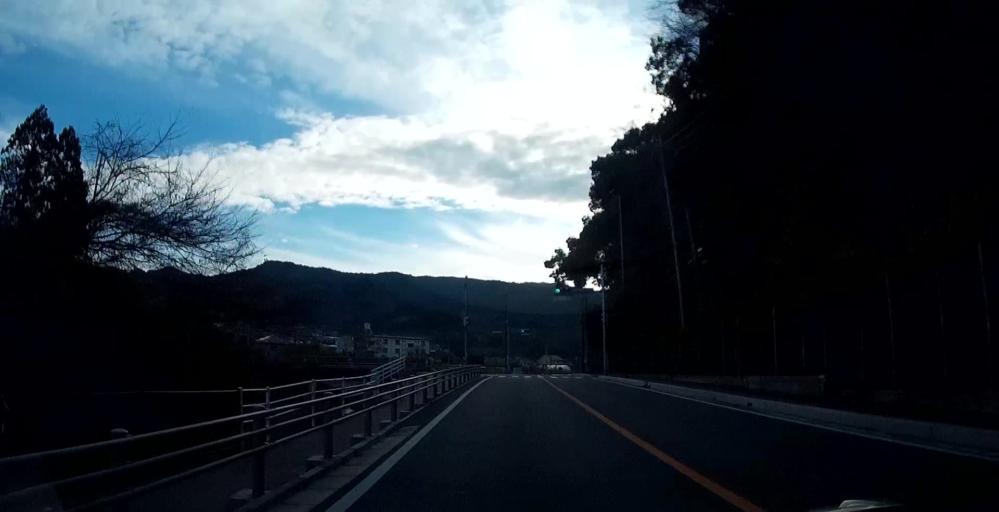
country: JP
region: Kumamoto
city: Uto
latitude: 32.6703
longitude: 130.5516
